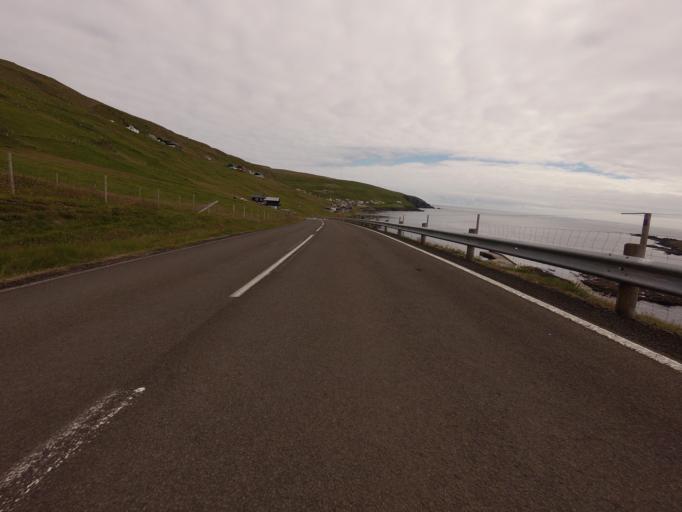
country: FO
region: Suduroy
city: Vagur
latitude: 61.4073
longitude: -6.7310
